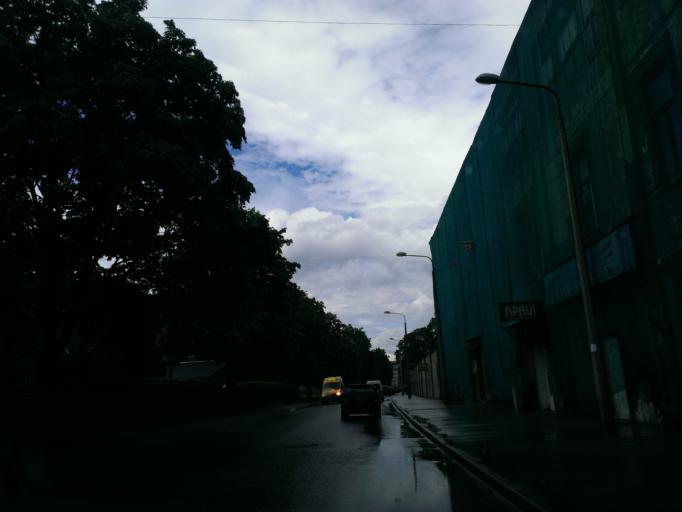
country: LV
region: Riga
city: Riga
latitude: 56.9226
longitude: 24.0954
